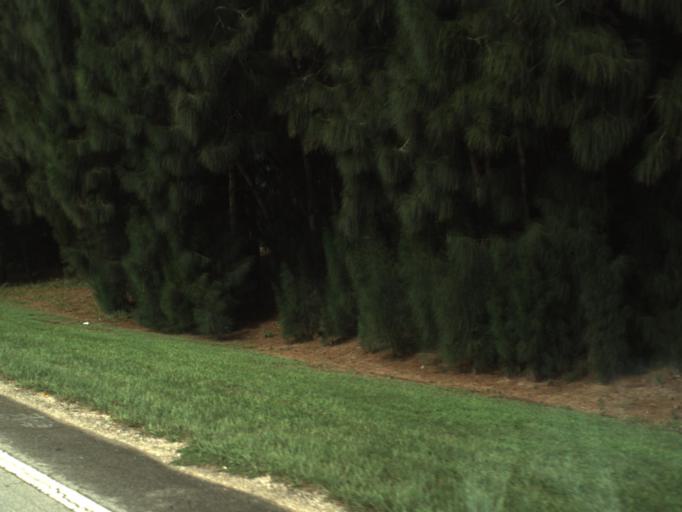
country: US
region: Florida
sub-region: Miami-Dade County
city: Naranja
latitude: 25.5409
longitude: -80.4780
